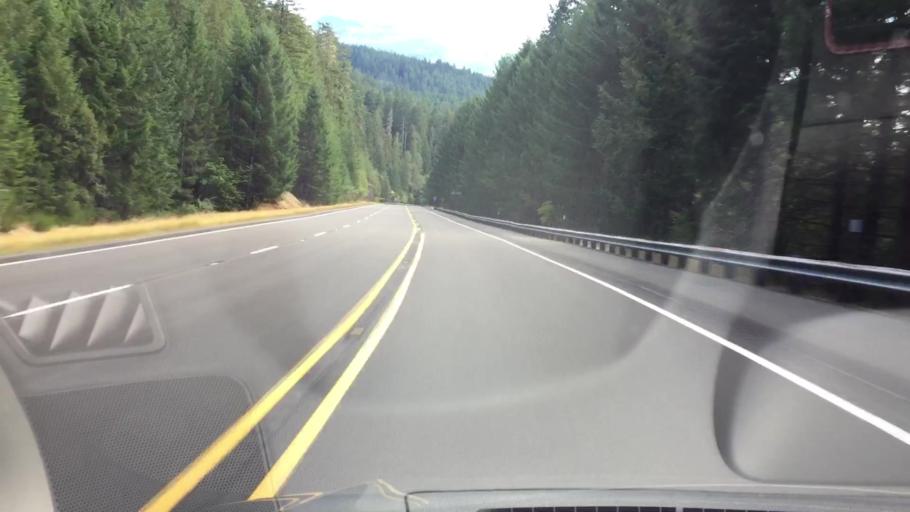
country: US
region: Washington
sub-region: Pierce County
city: Buckley
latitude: 46.6598
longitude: -121.6014
